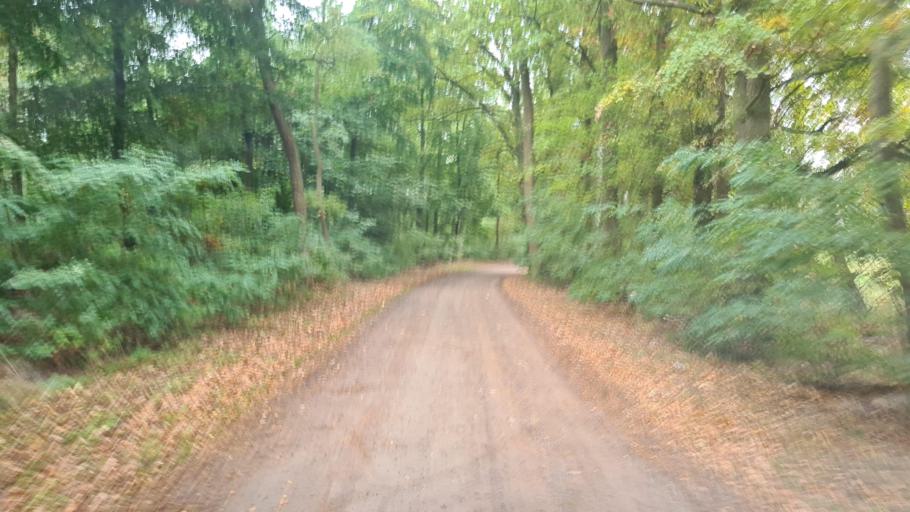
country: DE
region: Brandenburg
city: Storkow
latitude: 52.2279
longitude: 13.9340
